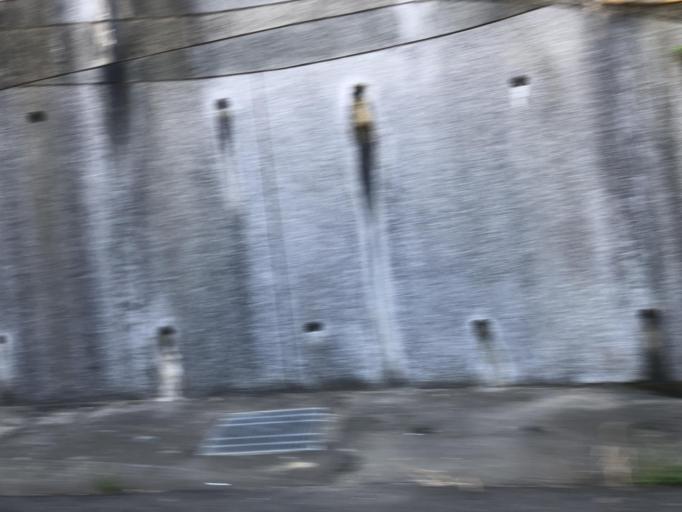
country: TW
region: Taiwan
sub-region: Tainan
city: Tainan
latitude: 23.0363
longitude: 120.3423
